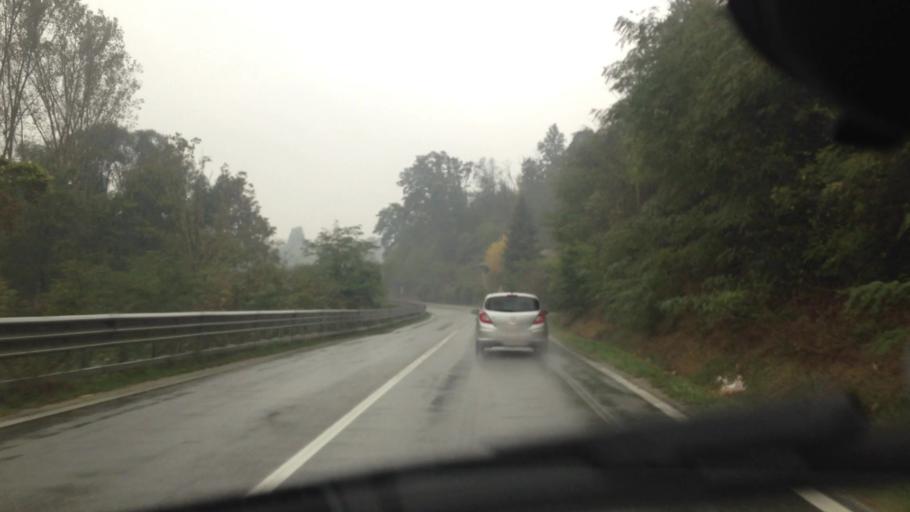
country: IT
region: Piedmont
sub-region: Provincia di Asti
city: Castello di Annone
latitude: 44.8870
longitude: 8.3096
